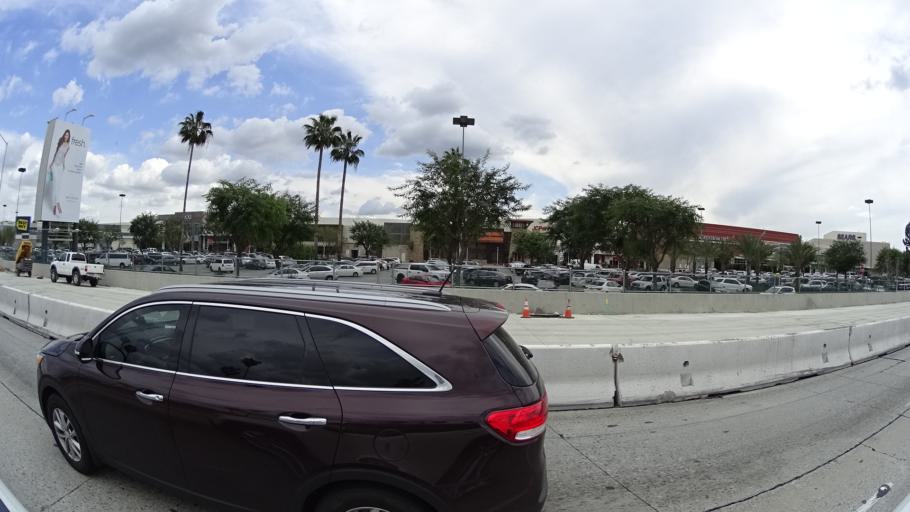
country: US
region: California
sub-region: Los Angeles County
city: West Covina
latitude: 34.0722
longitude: -117.9326
